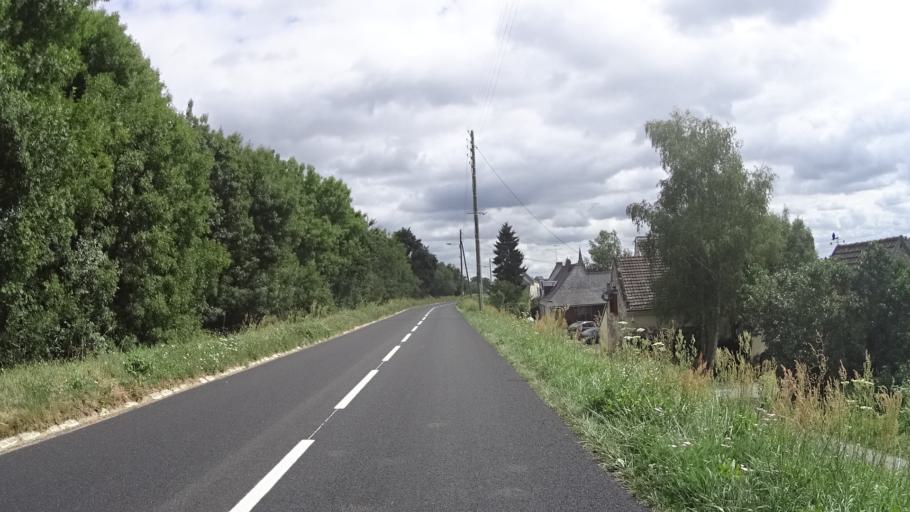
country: FR
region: Centre
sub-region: Departement d'Indre-et-Loire
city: Langeais
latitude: 47.2933
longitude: 0.3492
